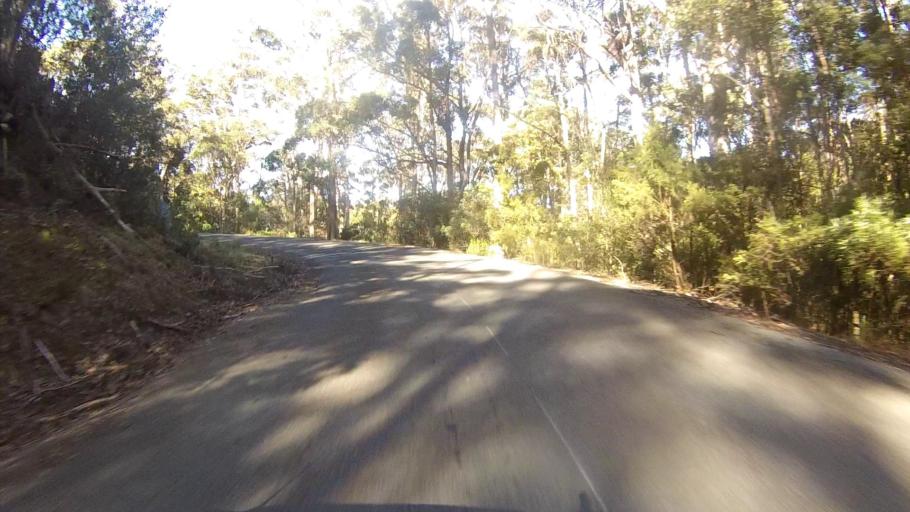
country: AU
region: Tasmania
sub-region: Sorell
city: Sorell
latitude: -43.0037
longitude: 147.9337
